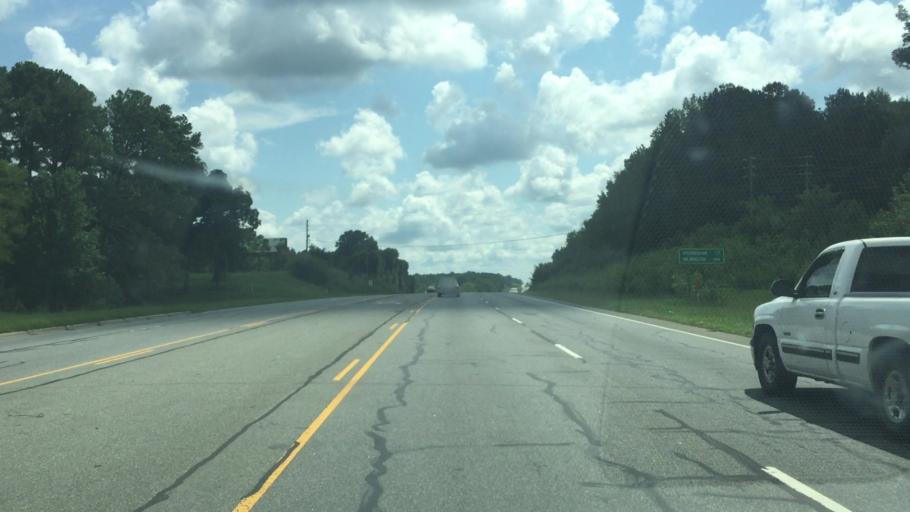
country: US
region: North Carolina
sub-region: Anson County
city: Wadesboro
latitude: 34.9637
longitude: -80.0295
